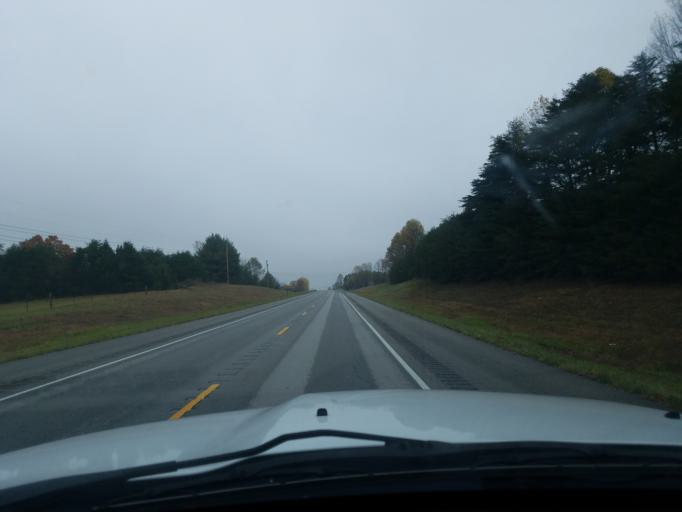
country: US
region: Kentucky
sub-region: Green County
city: Greensburg
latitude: 37.4056
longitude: -85.4810
